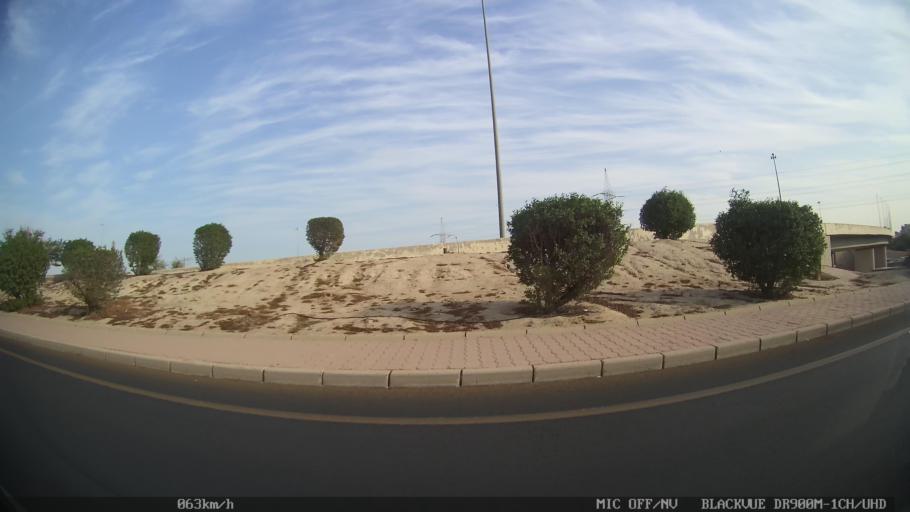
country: KW
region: Al Farwaniyah
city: Al Farwaniyah
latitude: 29.3057
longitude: 47.9771
